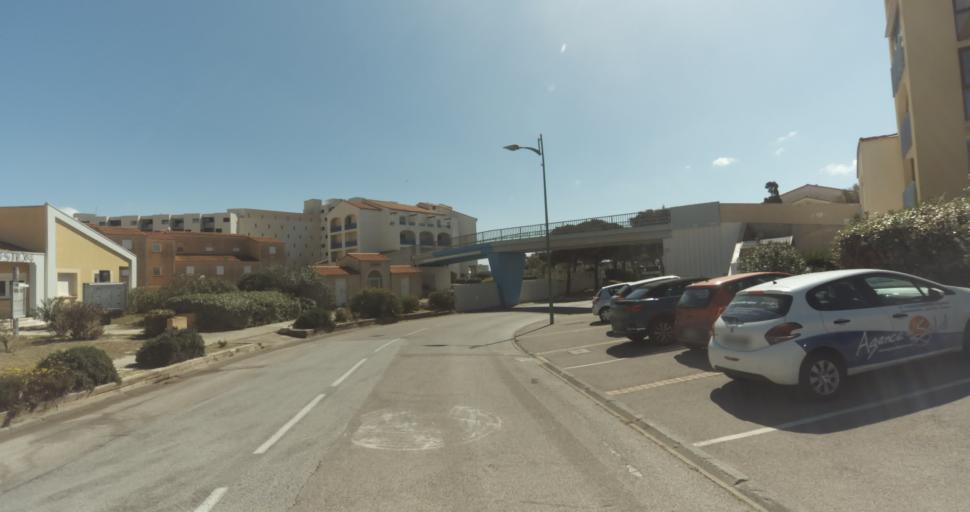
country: FR
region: Languedoc-Roussillon
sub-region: Departement des Pyrenees-Orientales
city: Le Barcares
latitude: 42.8324
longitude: 3.0397
